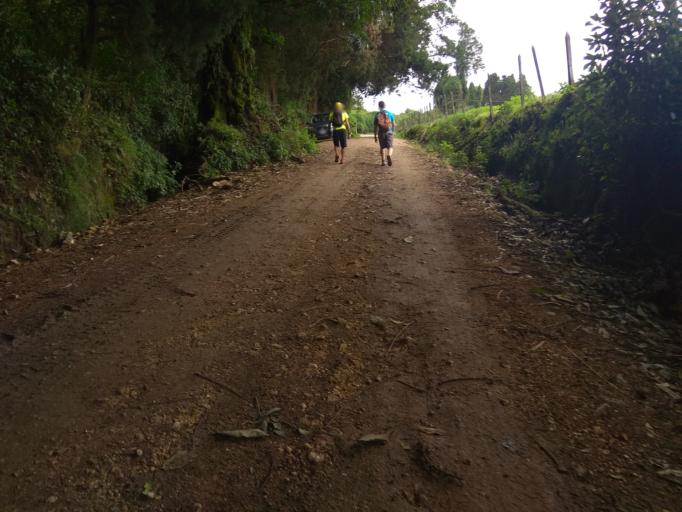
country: CR
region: Cartago
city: Cot
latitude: 9.9523
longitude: -83.8839
